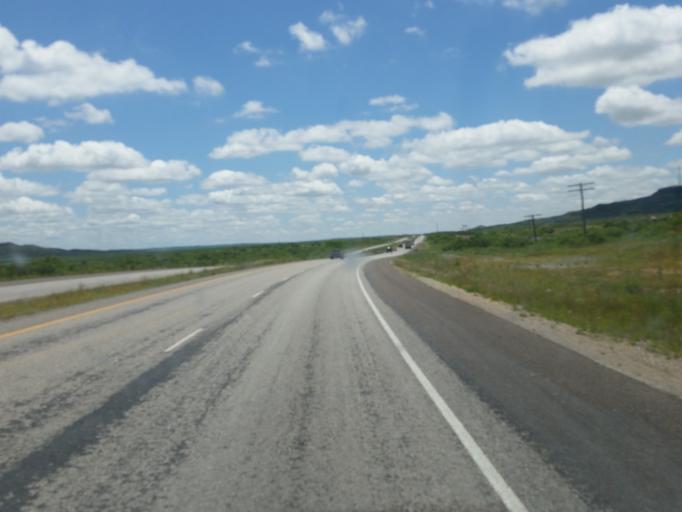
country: US
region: Texas
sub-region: Scurry County
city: Snyder
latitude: 32.9776
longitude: -101.1039
